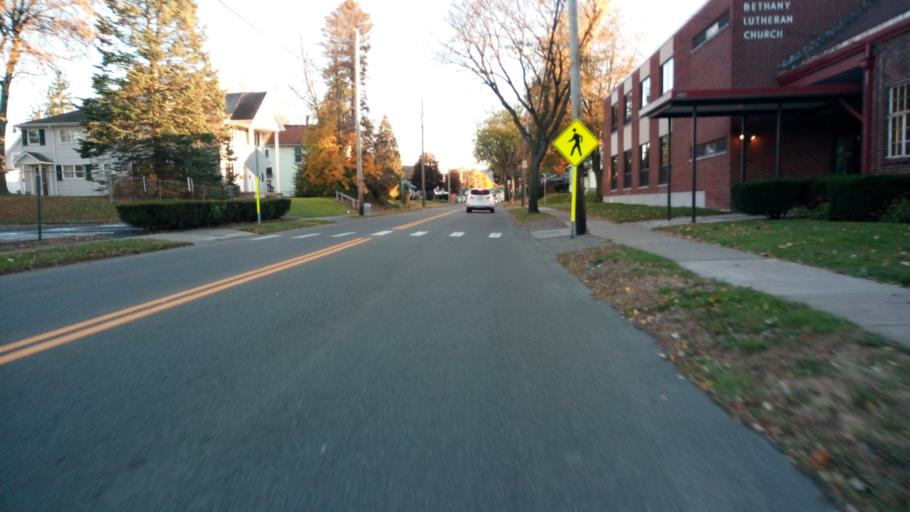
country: US
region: New York
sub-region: Chemung County
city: Elmira
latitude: 42.0796
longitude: -76.8137
